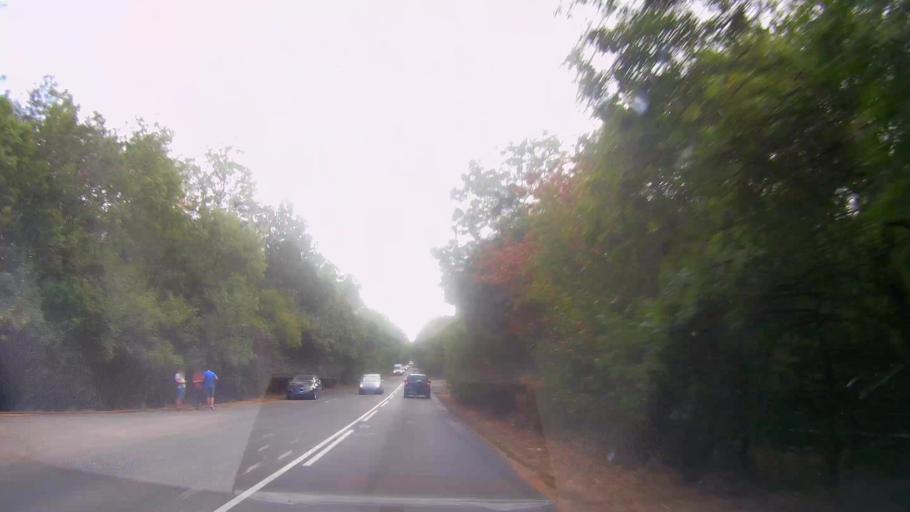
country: BG
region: Burgas
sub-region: Obshtina Primorsko
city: Primorsko
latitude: 42.3007
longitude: 27.7293
